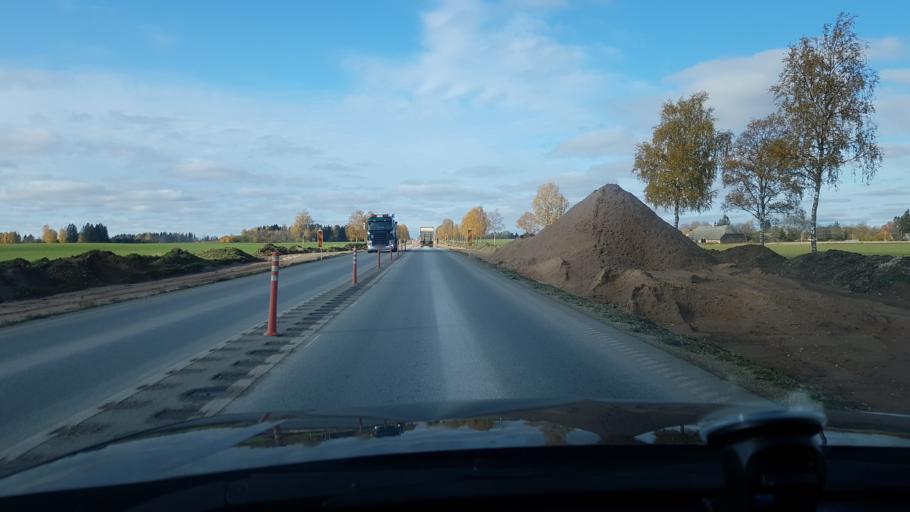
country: EE
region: Laeaene-Virumaa
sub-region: Haljala vald
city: Haljala
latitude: 59.4320
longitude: 26.1974
